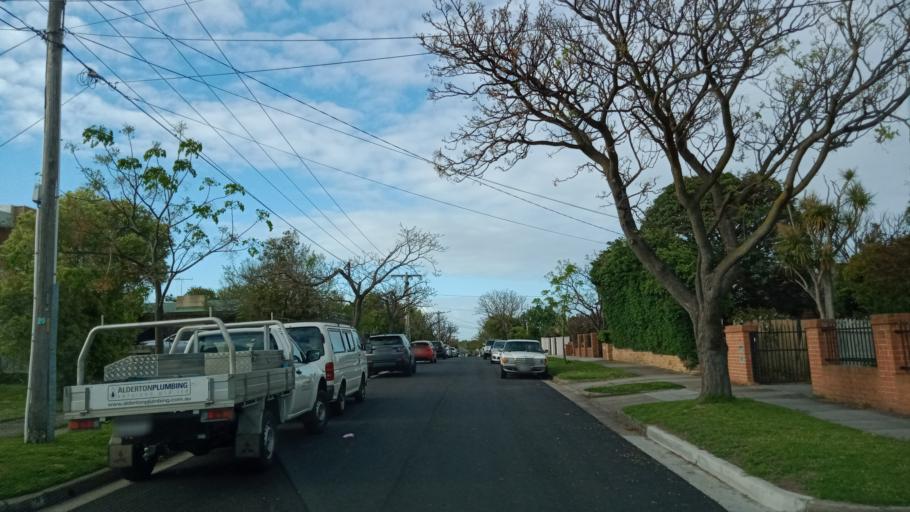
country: AU
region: Victoria
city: McKinnon
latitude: -37.9304
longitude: 145.0558
